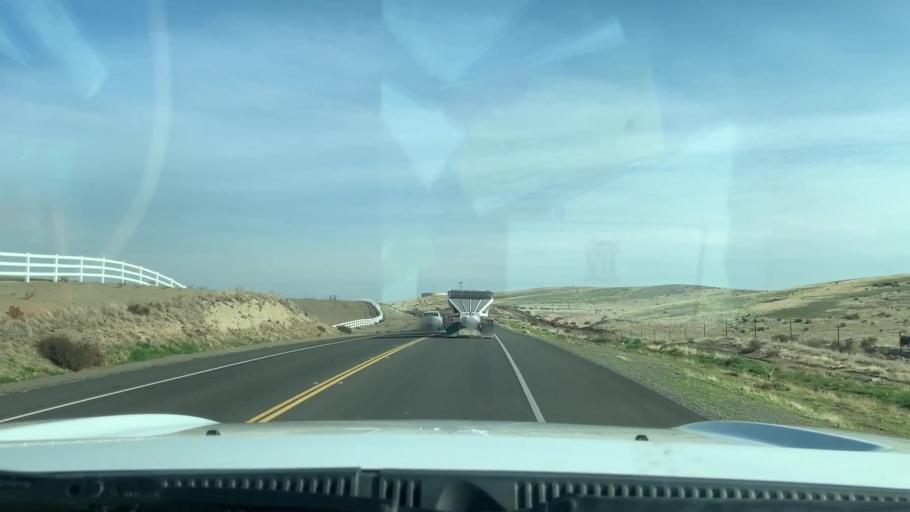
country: US
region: California
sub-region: Fresno County
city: Coalinga
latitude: 36.2033
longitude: -120.3189
